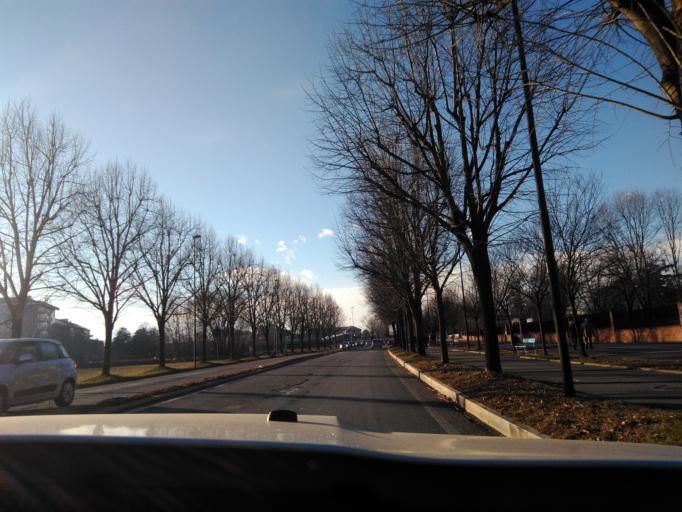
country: IT
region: Piedmont
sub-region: Provincia di Torino
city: Grugliasco
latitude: 45.0641
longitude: 7.5906
